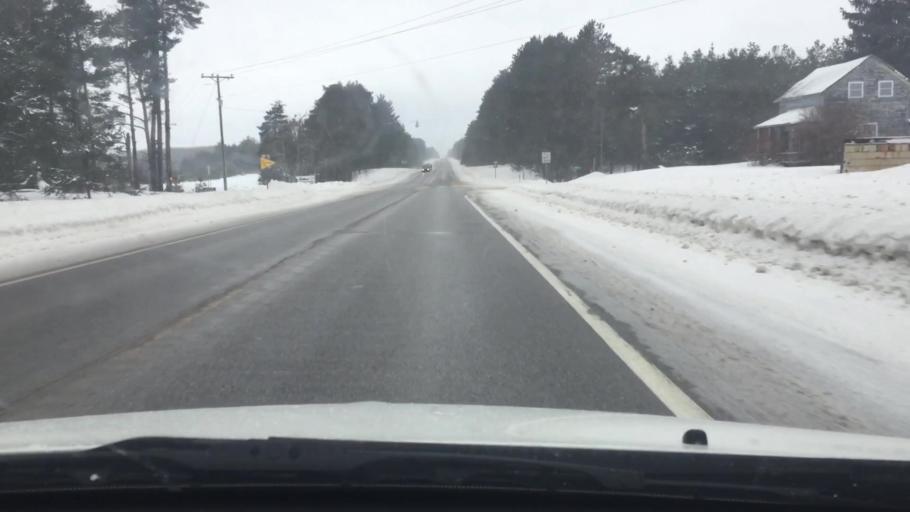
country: US
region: Michigan
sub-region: Otsego County
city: Gaylord
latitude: 45.0619
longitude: -84.8156
